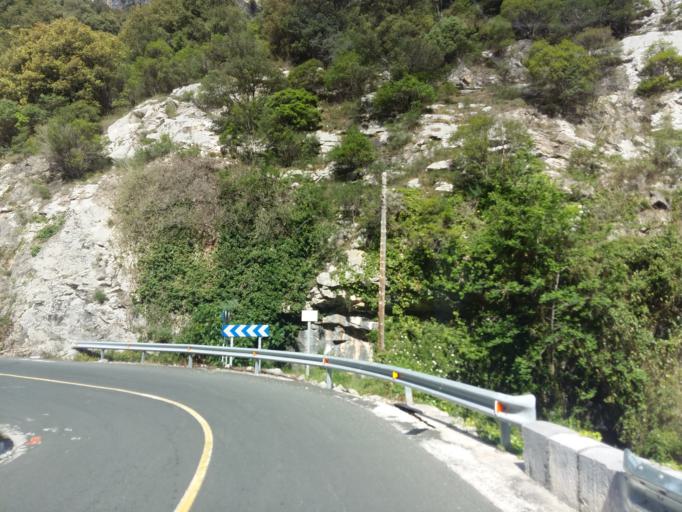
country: ES
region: Cantabria
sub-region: Provincia de Cantabria
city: Potes
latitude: 43.2277
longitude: -4.5832
